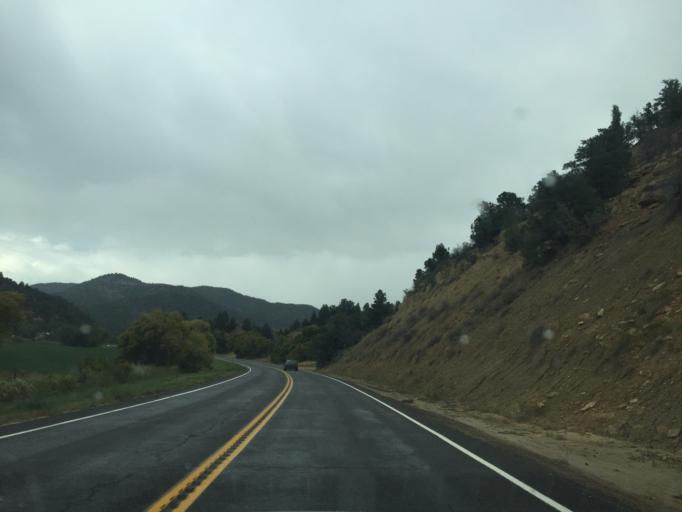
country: US
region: Utah
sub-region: Kane County
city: Kanab
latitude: 37.3303
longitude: -112.5998
